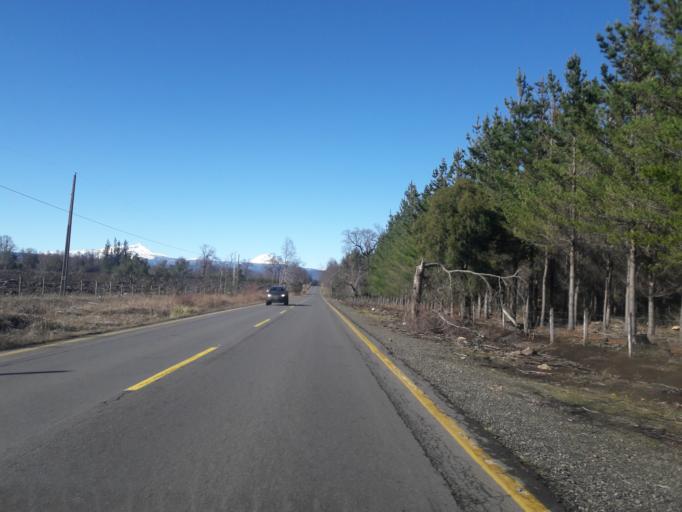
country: CL
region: Araucania
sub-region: Provincia de Malleco
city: Victoria
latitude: -38.3286
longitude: -71.9910
